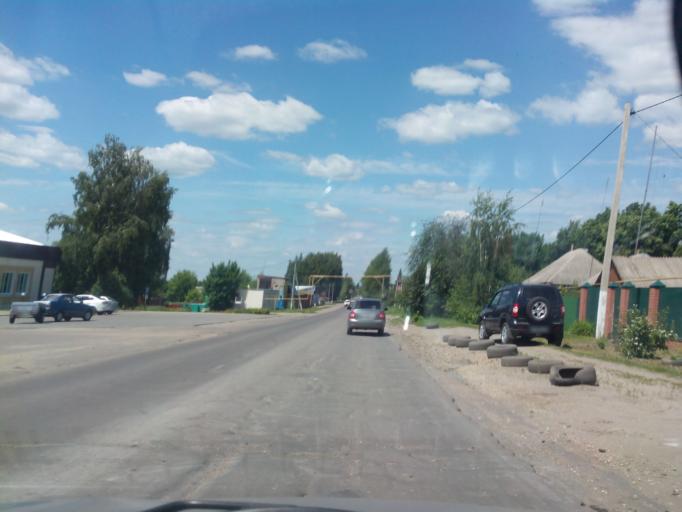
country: RU
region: Tambov
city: Zherdevka
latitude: 51.8193
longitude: 41.5070
